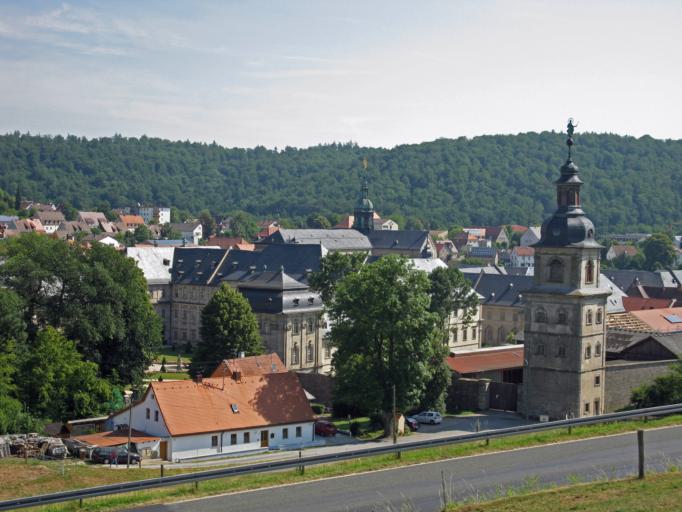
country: DE
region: Bavaria
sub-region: Regierungsbezirk Unterfranken
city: Geiselwind
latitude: 49.8453
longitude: 10.4907
